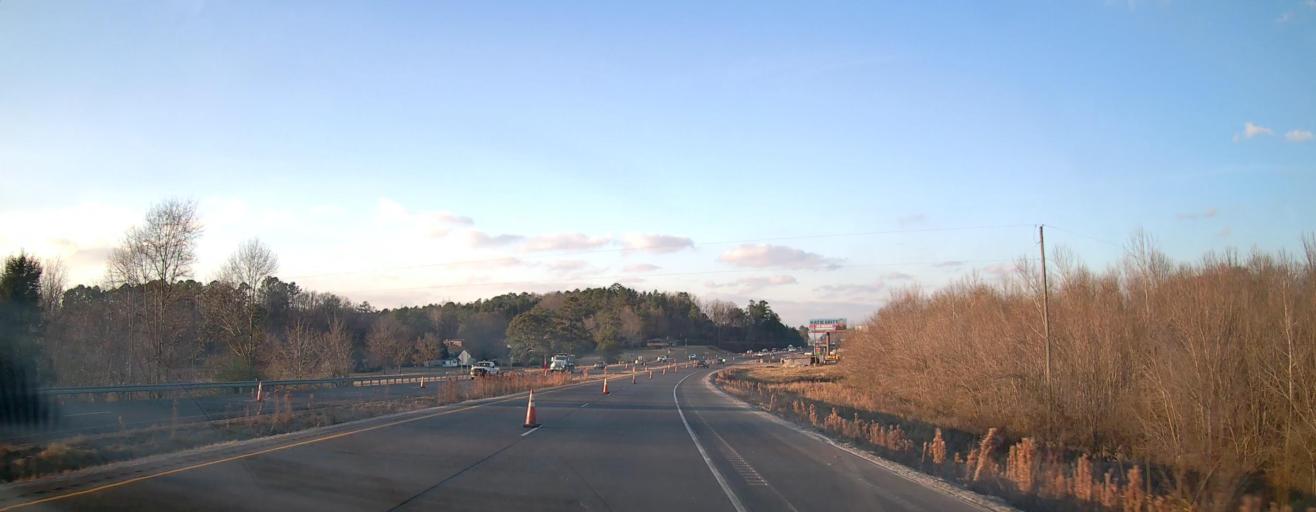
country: US
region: Alabama
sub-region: Calhoun County
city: Saks
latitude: 33.7227
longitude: -85.8758
